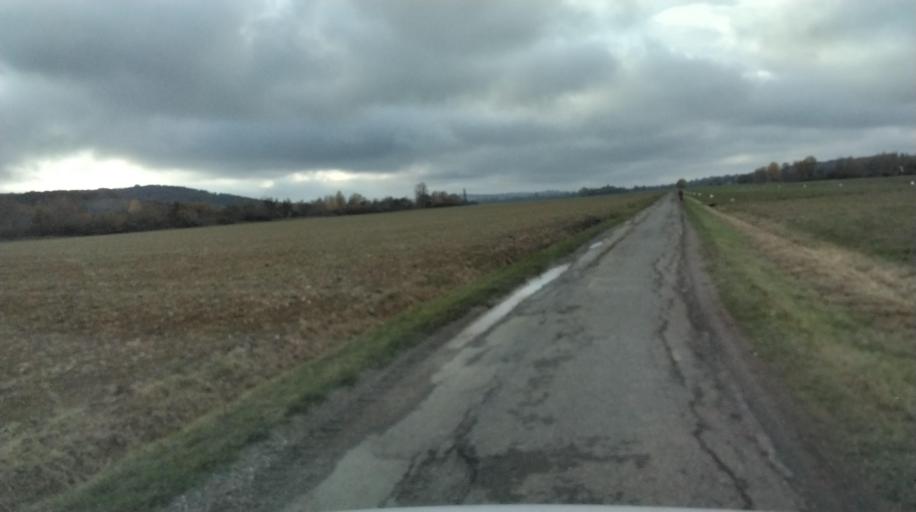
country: FR
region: Midi-Pyrenees
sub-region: Departement de la Haute-Garonne
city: Le Fousseret
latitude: 43.2683
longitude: 1.0576
